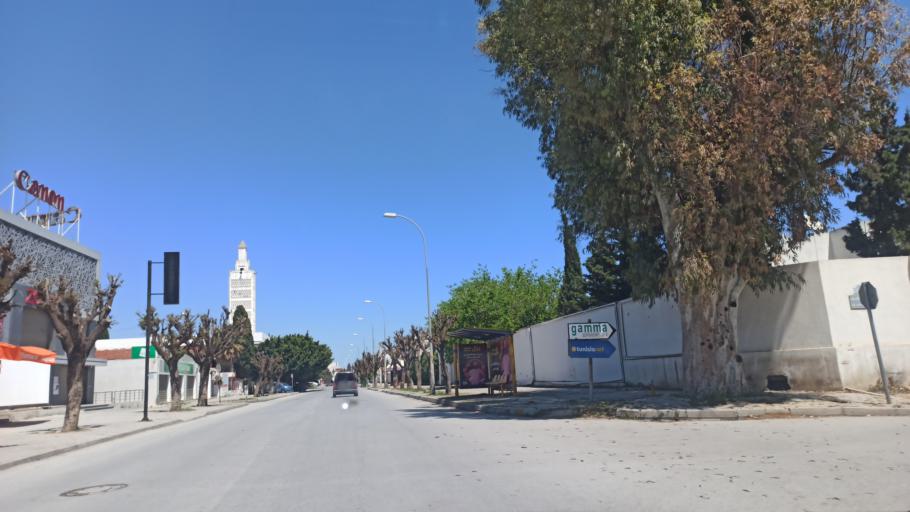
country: TN
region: Tunis
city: Tunis
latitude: 36.8259
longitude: 10.1827
